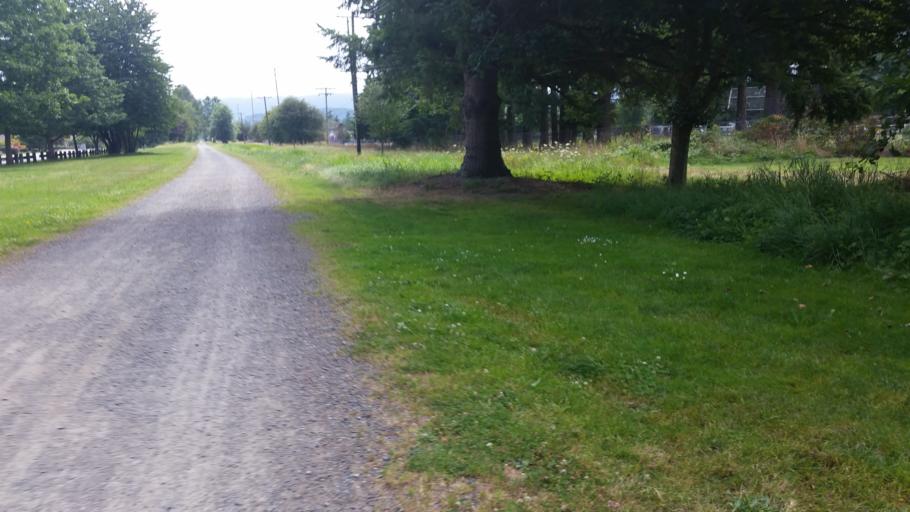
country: US
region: Washington
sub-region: King County
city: North Bend
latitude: 47.4965
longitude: -121.7811
